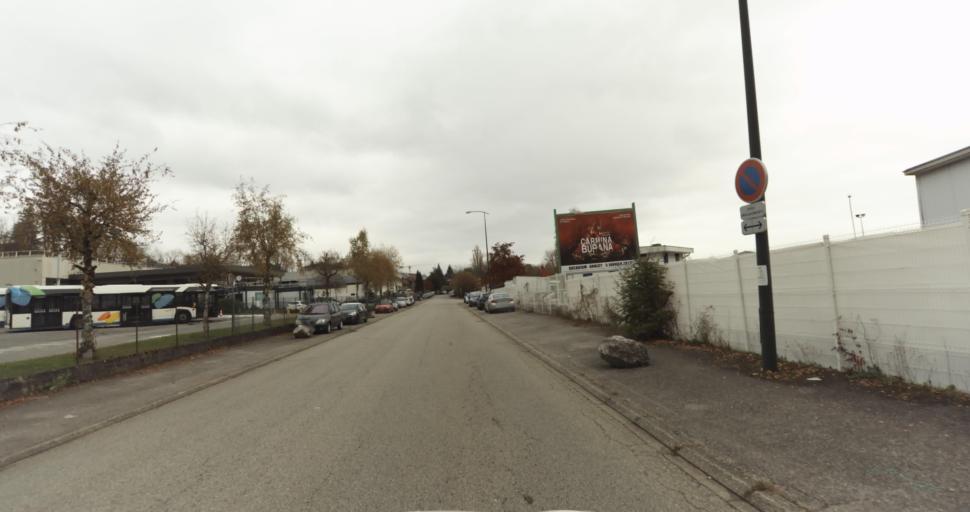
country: FR
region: Rhone-Alpes
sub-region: Departement de la Haute-Savoie
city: Annecy
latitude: 45.8838
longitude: 6.1124
